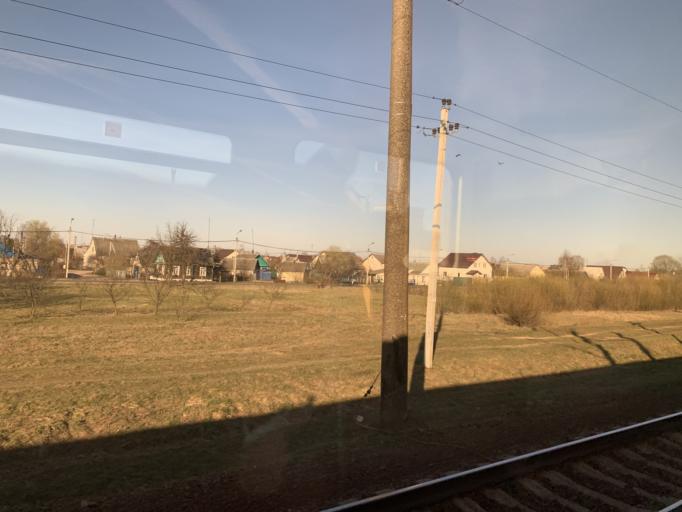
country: BY
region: Minsk
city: Maladzyechna
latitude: 54.3126
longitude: 26.8576
